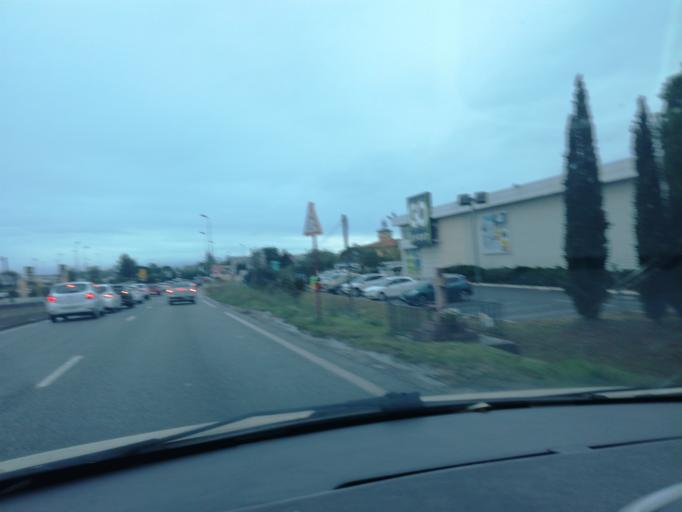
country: FR
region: Provence-Alpes-Cote d'Azur
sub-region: Departement du Var
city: Puget-sur-Argens
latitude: 43.4448
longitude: 6.7000
